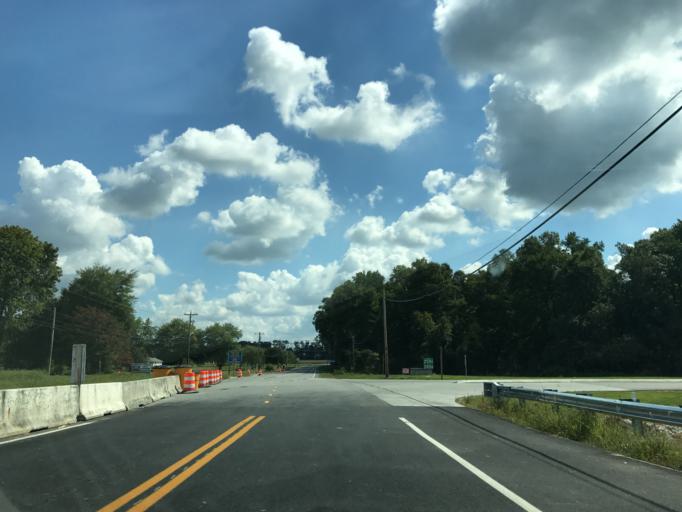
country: US
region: Maryland
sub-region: Queen Anne's County
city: Centreville
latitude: 39.0267
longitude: -76.0233
